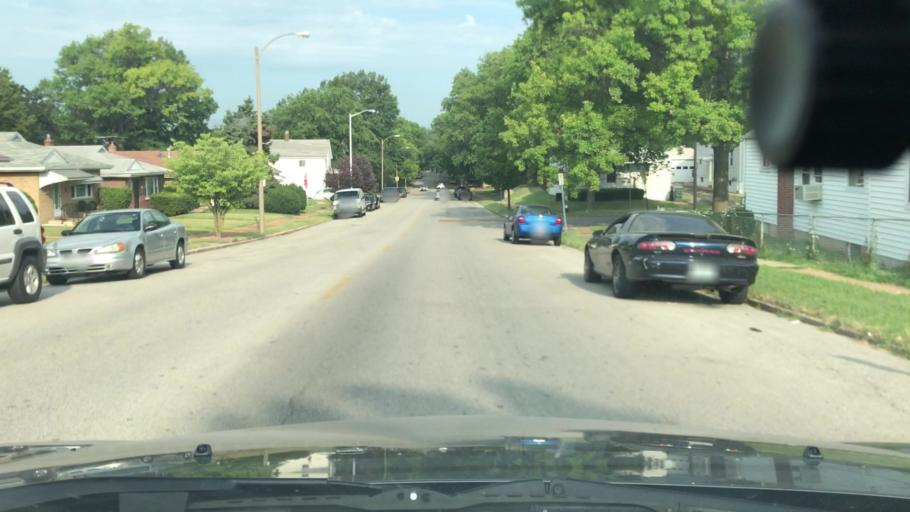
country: US
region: Missouri
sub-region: Saint Louis County
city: Maplewood
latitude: 38.6013
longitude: -90.2850
